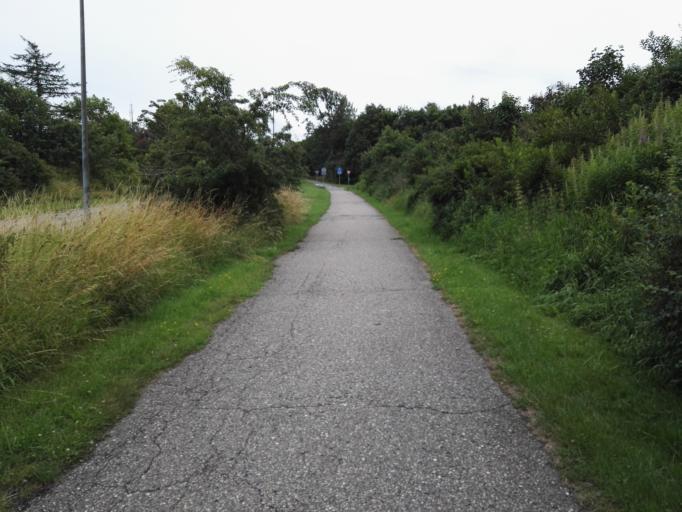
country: DK
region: Capital Region
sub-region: Egedal Kommune
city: Olstykke
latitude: 55.7751
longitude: 12.1622
